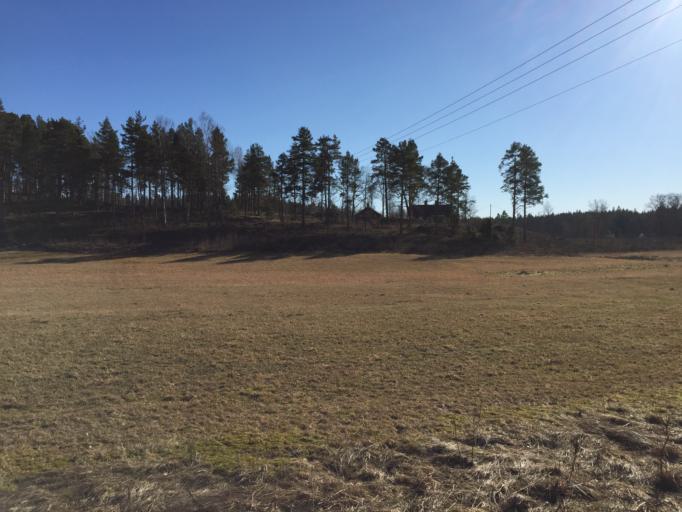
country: SE
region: Soedermanland
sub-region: Vingakers Kommun
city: Vingaker
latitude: 58.9039
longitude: 15.8497
